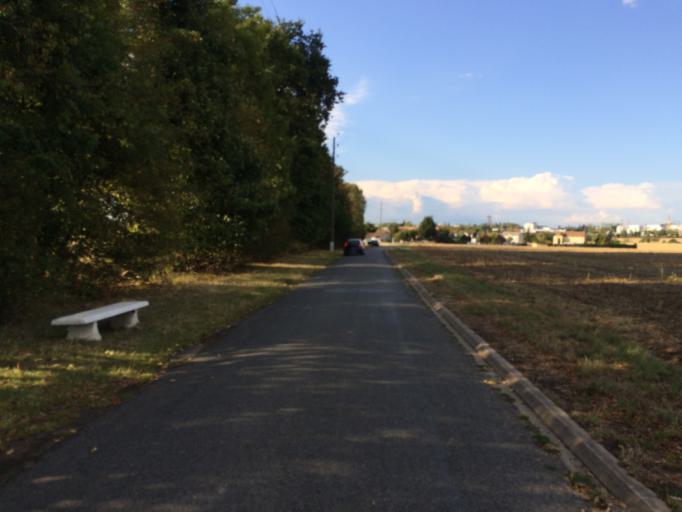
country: FR
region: Ile-de-France
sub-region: Departement de l'Essonne
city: Les Ulis
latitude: 48.6664
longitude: 2.1672
